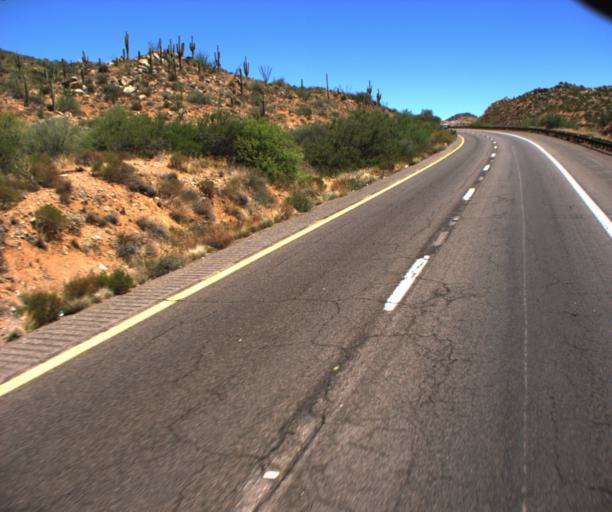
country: US
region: Arizona
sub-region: Gila County
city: Tonto Basin
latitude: 33.8180
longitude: -111.4787
